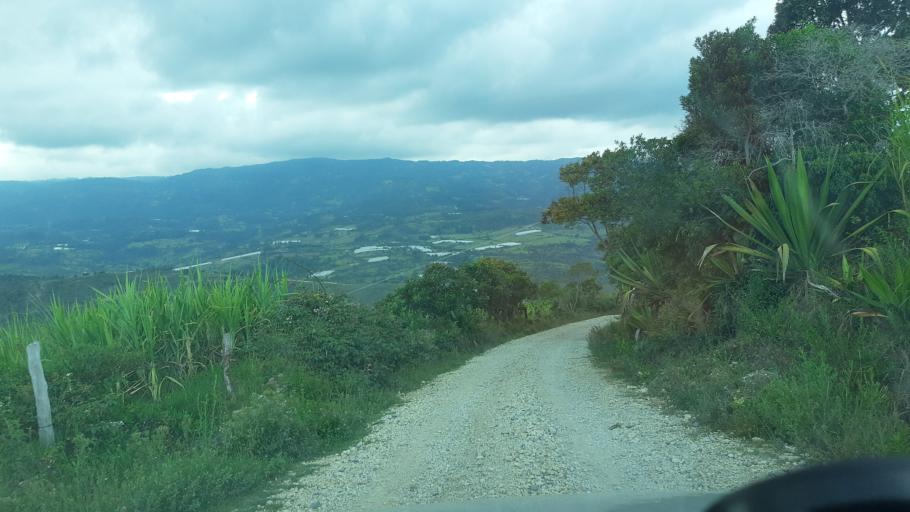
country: CO
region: Boyaca
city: Santa Sofia
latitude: 5.7460
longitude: -73.5681
